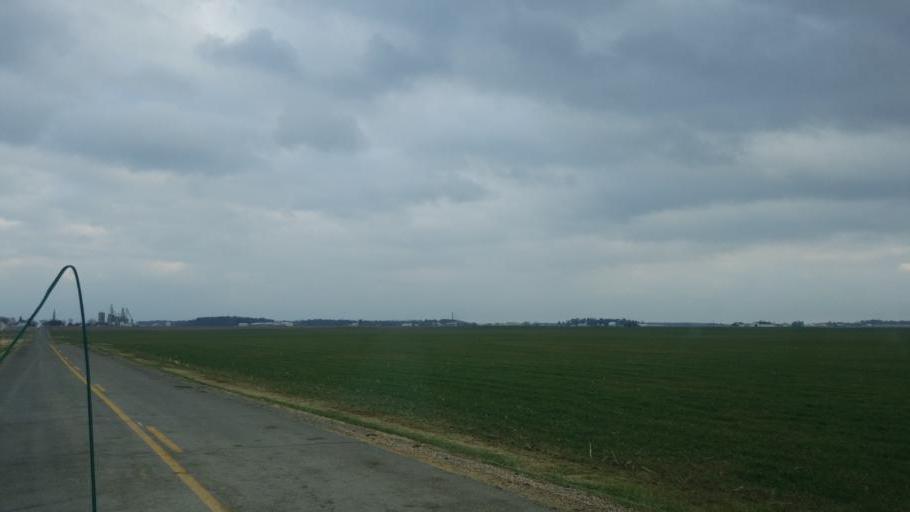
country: US
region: Ohio
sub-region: Mercer County
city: Fort Recovery
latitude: 40.5092
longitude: -84.8027
